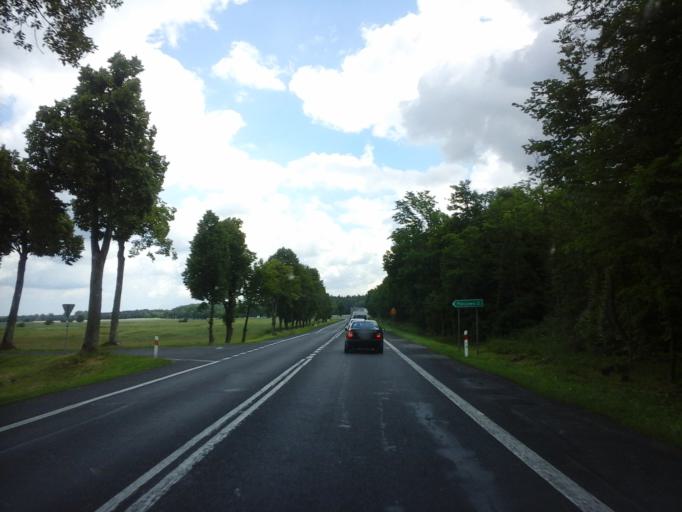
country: PL
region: West Pomeranian Voivodeship
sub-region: Powiat bialogardzki
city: Bialogard
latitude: 54.0798
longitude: 15.9752
